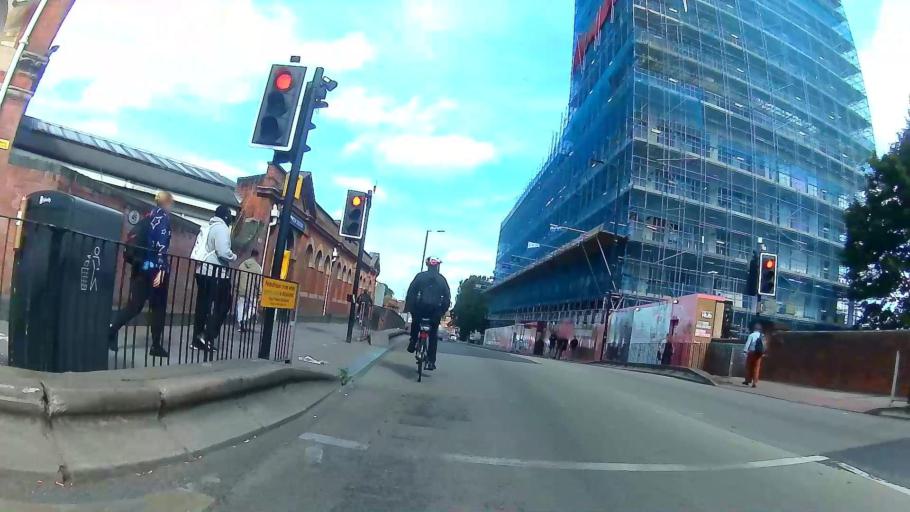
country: GB
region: England
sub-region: Greater London
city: East Ham
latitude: 51.5314
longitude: 0.0180
